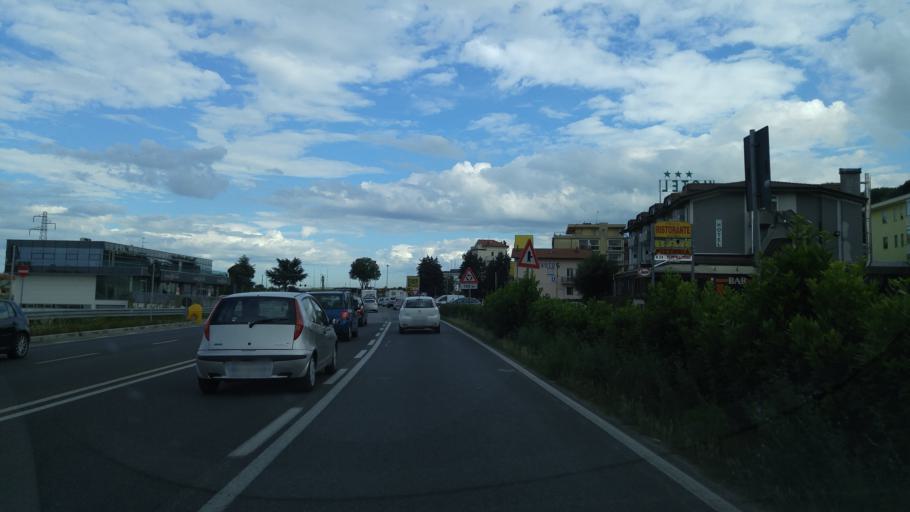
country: IT
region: Emilia-Romagna
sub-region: Provincia di Rimini
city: Rimini
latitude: 44.0476
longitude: 12.5507
